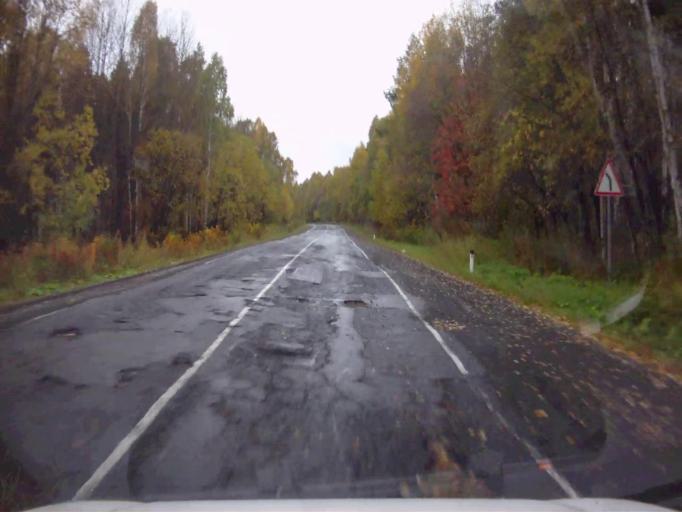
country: RU
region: Chelyabinsk
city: Nizhniy Ufaley
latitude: 56.0545
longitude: 60.0543
